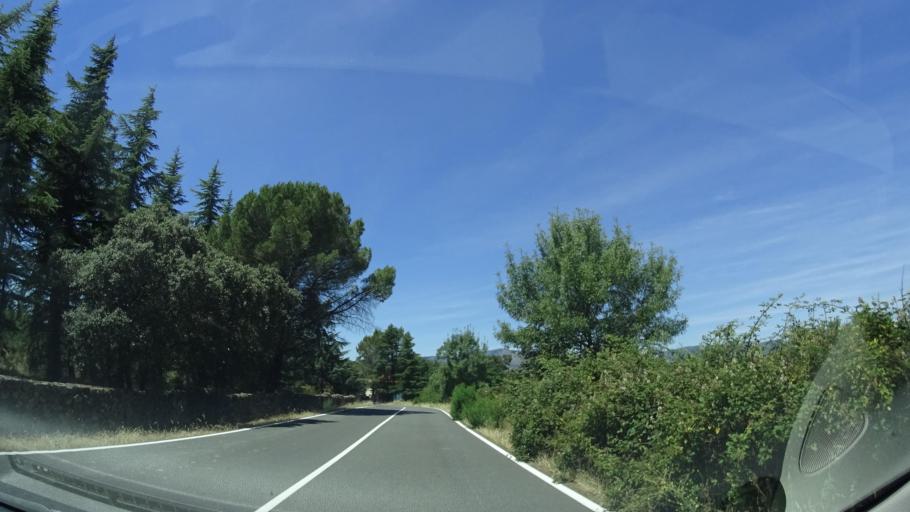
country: ES
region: Madrid
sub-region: Provincia de Madrid
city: Galapagar
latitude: 40.6064
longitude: -3.9801
